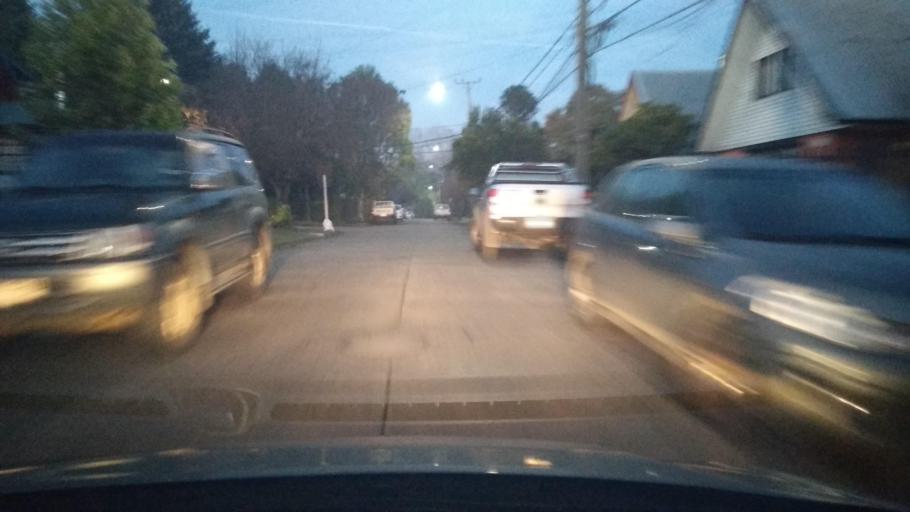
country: CL
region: Los Rios
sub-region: Provincia de Valdivia
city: Valdivia
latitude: -39.8110
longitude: -73.2603
